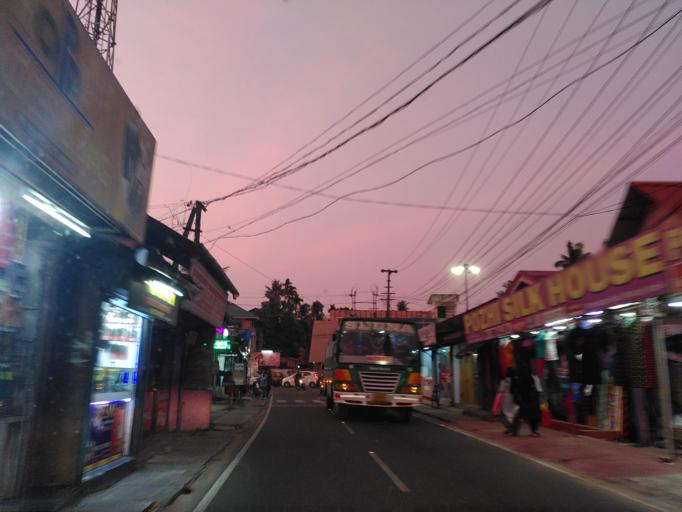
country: IN
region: Kerala
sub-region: Ernakulam
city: Cochin
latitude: 9.9134
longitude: 76.2790
